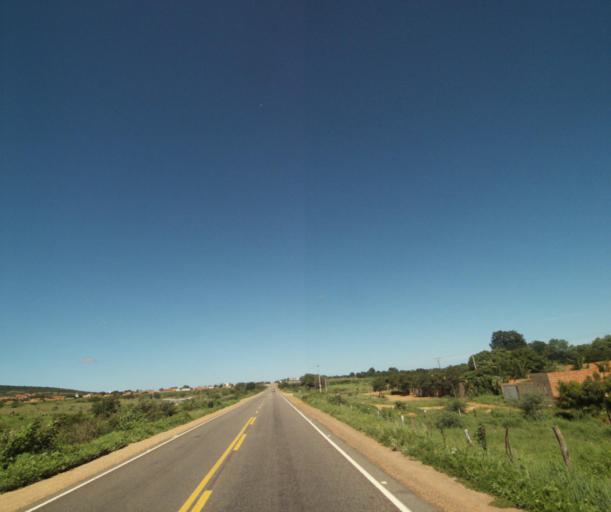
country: BR
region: Bahia
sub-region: Palmas De Monte Alto
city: Palmas de Monte Alto
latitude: -14.2493
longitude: -43.1601
